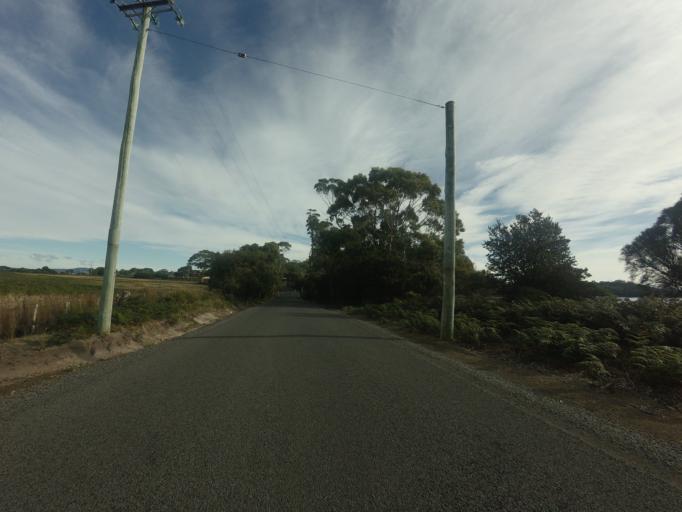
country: AU
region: Tasmania
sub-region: Sorell
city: Sorell
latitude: -42.9642
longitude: 147.8326
